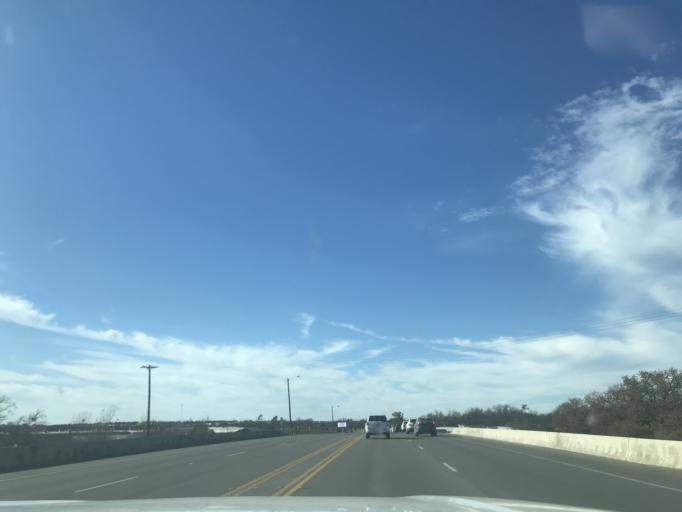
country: US
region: Texas
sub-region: Erath County
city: Stephenville
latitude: 32.2057
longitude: -98.2185
